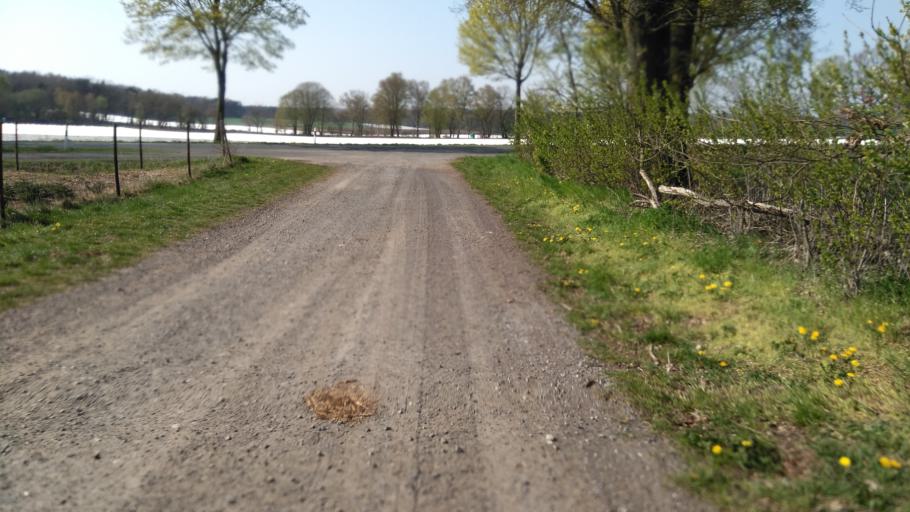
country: DE
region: Lower Saxony
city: Bliedersdorf
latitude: 53.4756
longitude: 9.5651
